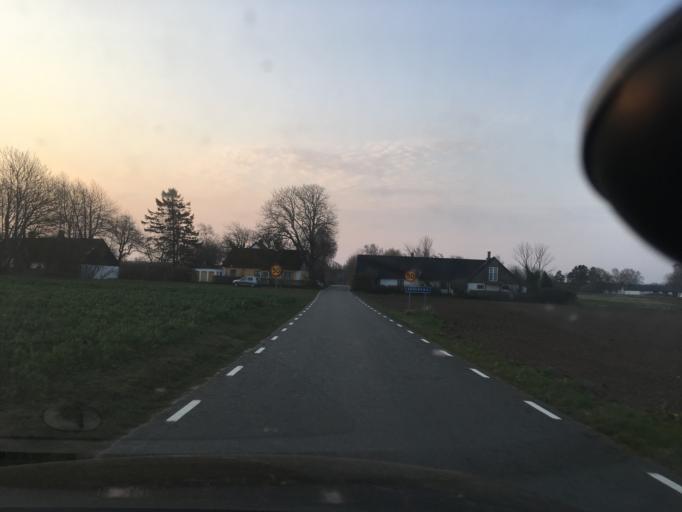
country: SE
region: Skane
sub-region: Ystads Kommun
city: Kopingebro
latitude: 55.4029
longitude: 14.1616
